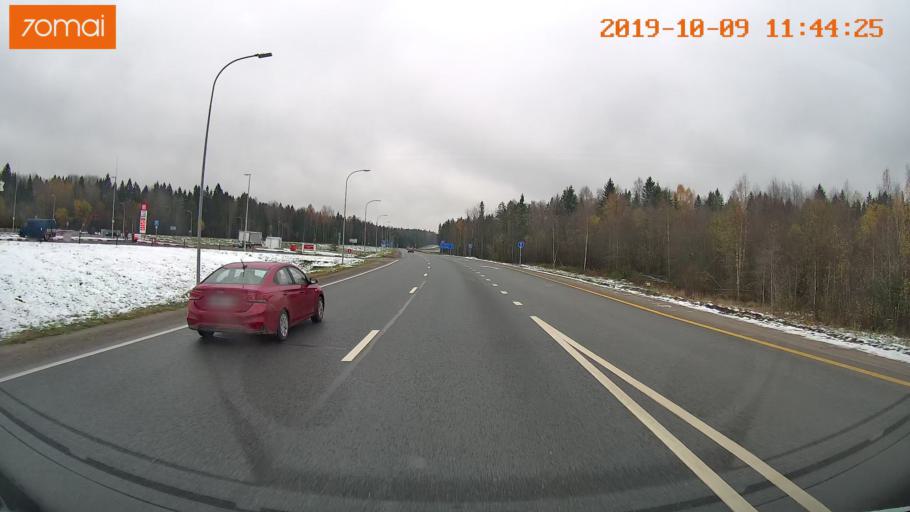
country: RU
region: Vologda
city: Gryazovets
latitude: 58.8835
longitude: 40.1905
